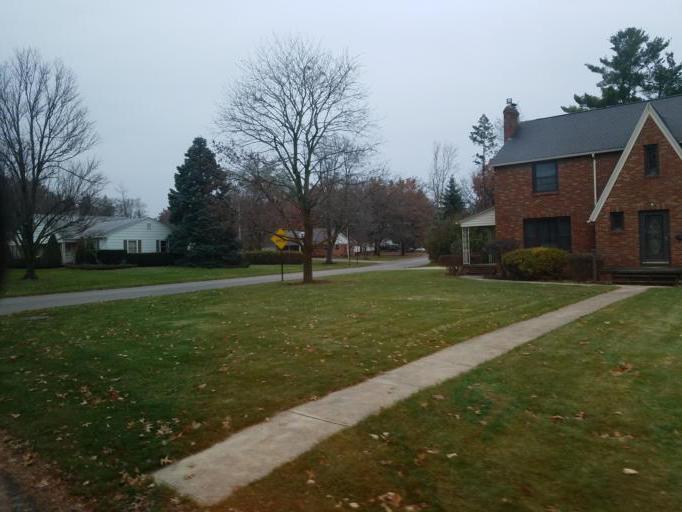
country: US
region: Ohio
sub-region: Richland County
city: Mansfield
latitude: 40.7358
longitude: -82.5393
